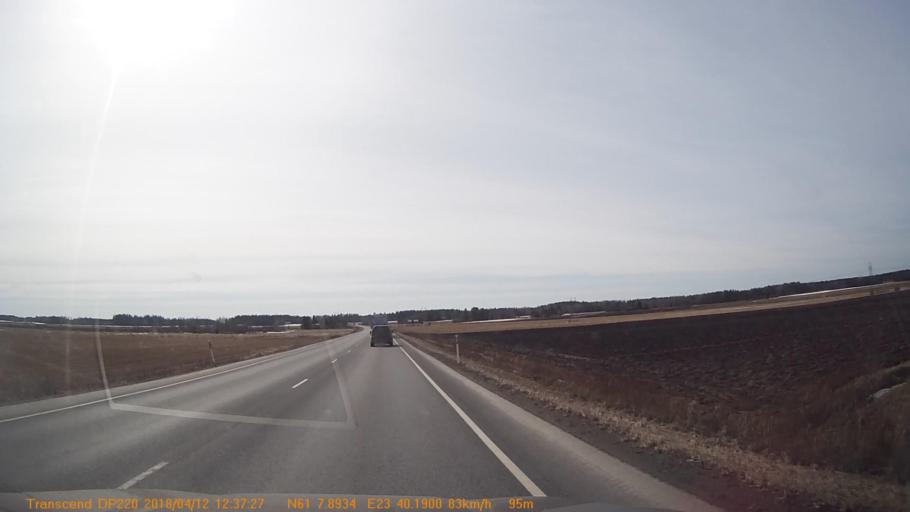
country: FI
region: Pirkanmaa
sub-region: Etelae-Pirkanmaa
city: Kylmaekoski
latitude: 61.1315
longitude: 23.6699
